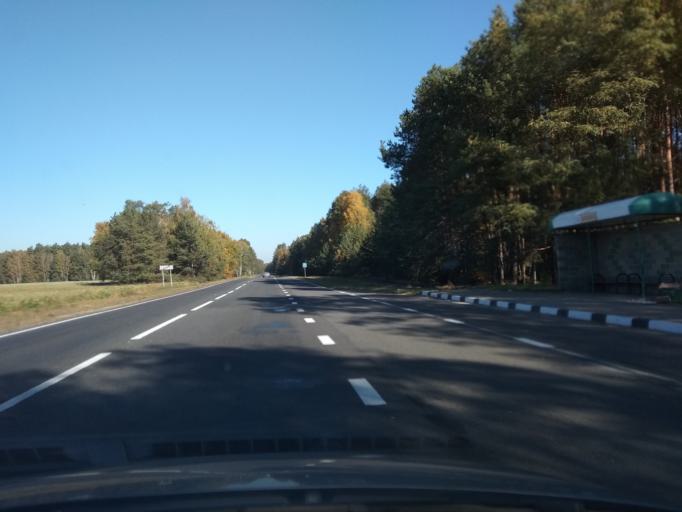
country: BY
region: Brest
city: Kobryn
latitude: 52.0552
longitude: 24.2799
